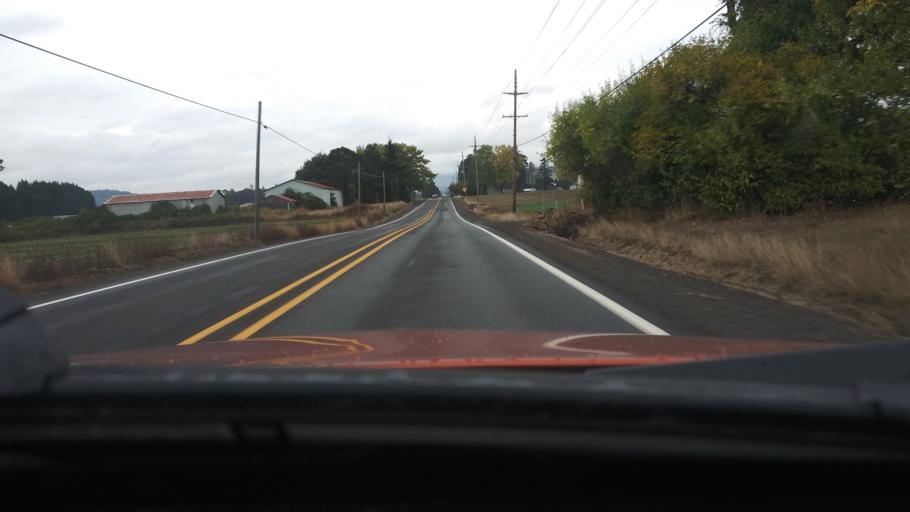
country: US
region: Oregon
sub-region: Washington County
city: Banks
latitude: 45.5989
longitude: -123.1145
